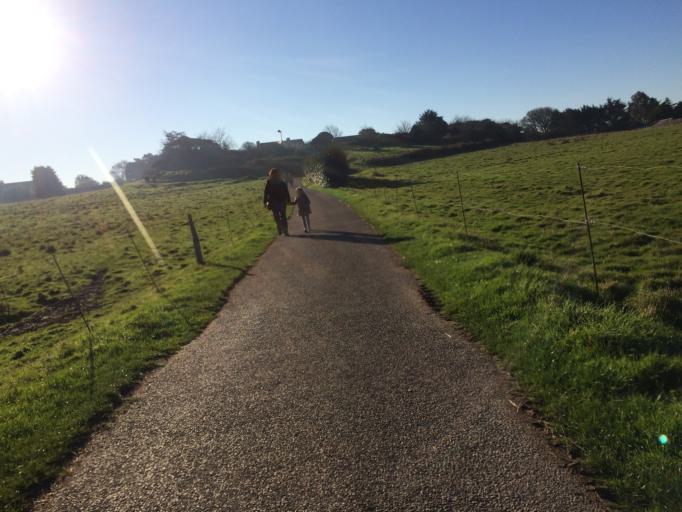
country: FR
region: Brittany
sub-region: Departement des Cotes-d'Armor
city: Ploubazlanec
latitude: 48.8569
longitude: -2.9971
